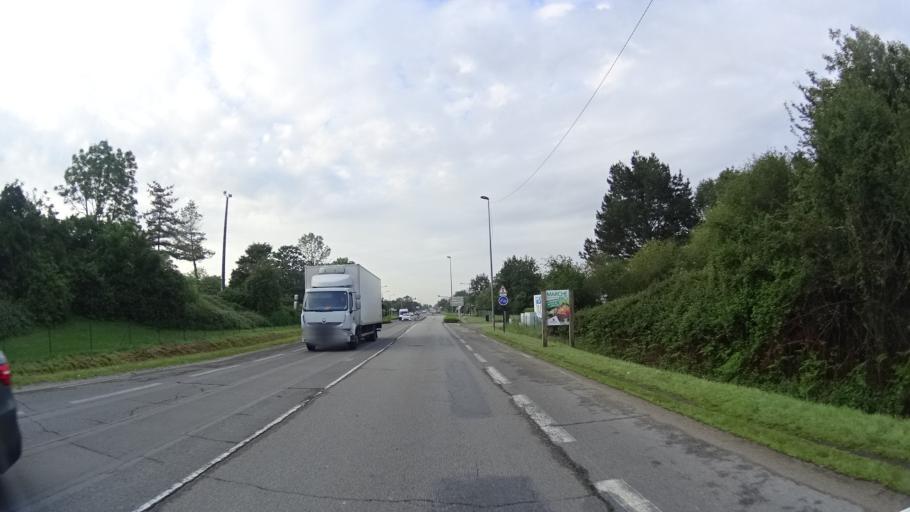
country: FR
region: Brittany
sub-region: Departement du Morbihan
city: Sene
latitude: 47.6473
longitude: -2.7232
